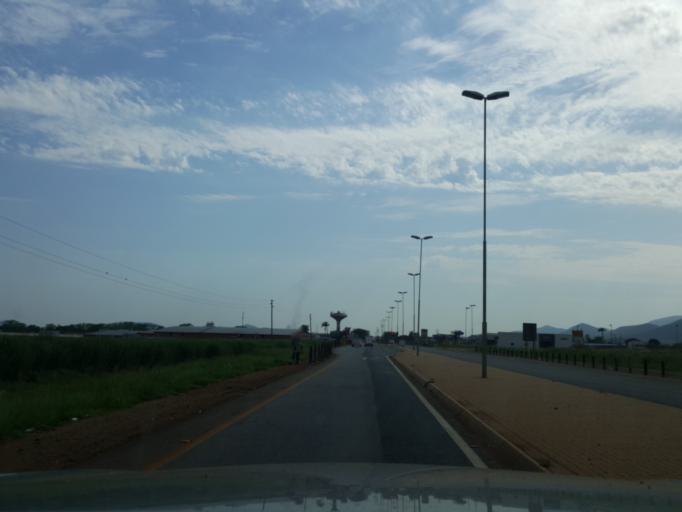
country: SZ
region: Hhohho
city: Ntfonjeni
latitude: -25.5026
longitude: 31.5024
